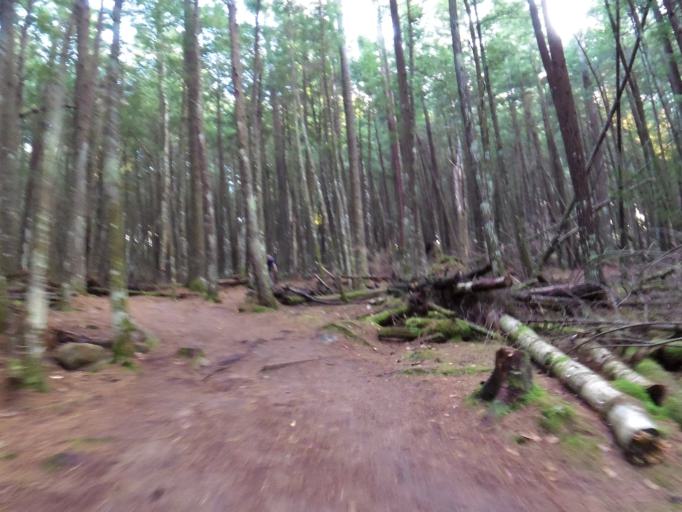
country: CA
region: Ontario
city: Deep River
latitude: 45.8886
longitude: -77.6359
